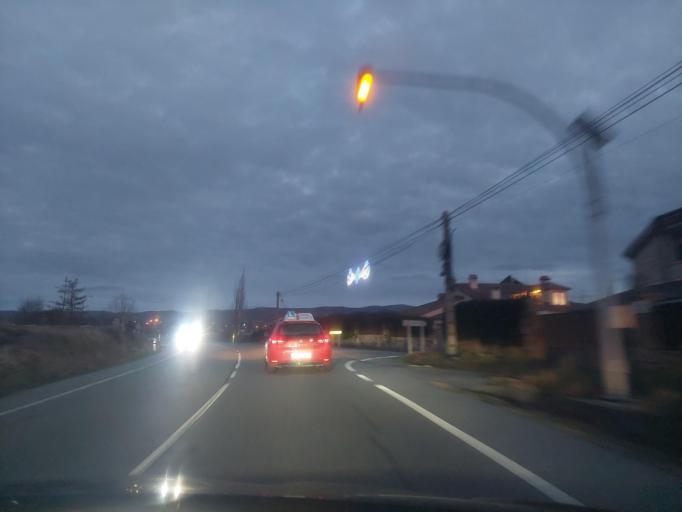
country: ES
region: Castille and Leon
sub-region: Provincia de Segovia
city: La Lastrilla
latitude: 40.9524
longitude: -4.1011
